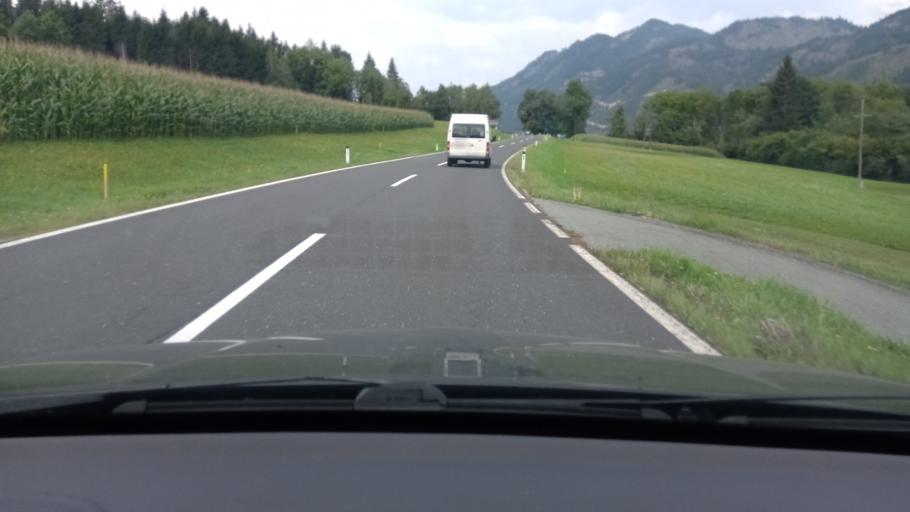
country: AT
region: Carinthia
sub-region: Politischer Bezirk Hermagor
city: Hermagor
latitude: 46.6559
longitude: 13.3204
